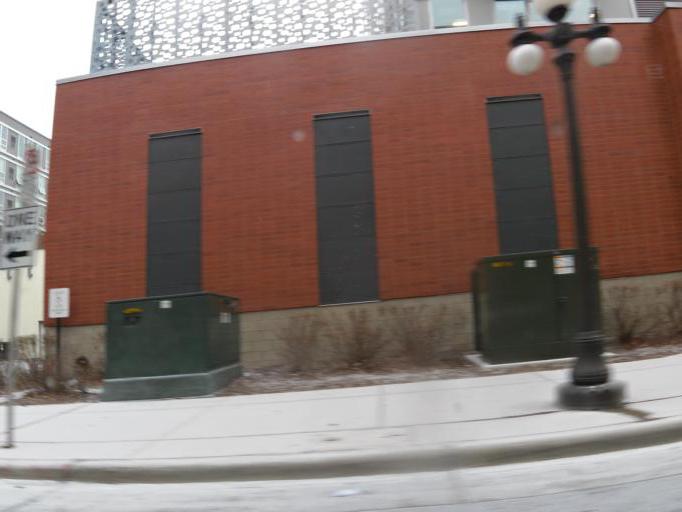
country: US
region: Minnesota
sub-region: Ramsey County
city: Saint Paul
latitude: 44.9511
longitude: -93.0960
